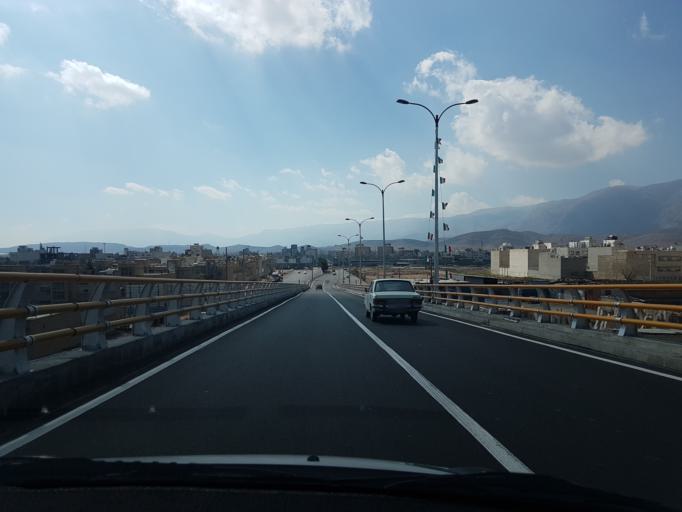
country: IR
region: Fars
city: Shiraz
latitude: 29.6109
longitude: 52.4678
